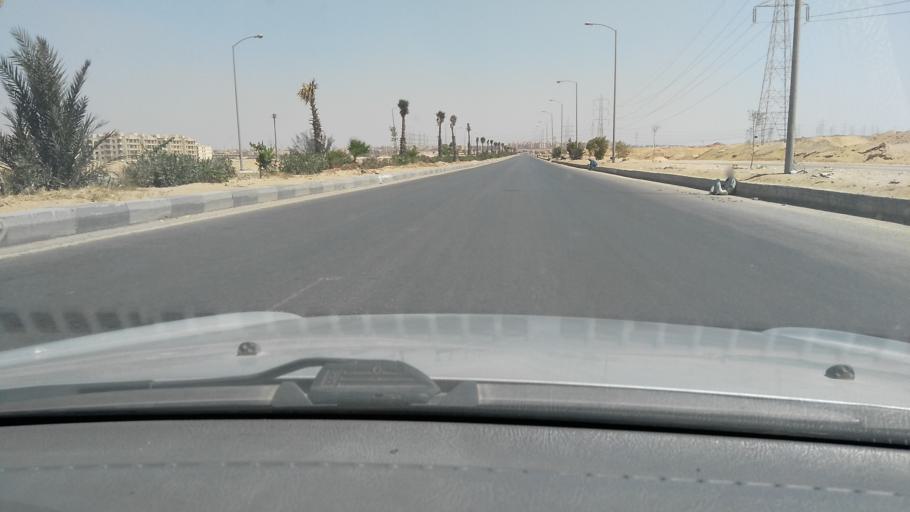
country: EG
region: Al Jizah
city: Madinat Sittah Uktubar
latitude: 29.9367
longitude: 30.9459
